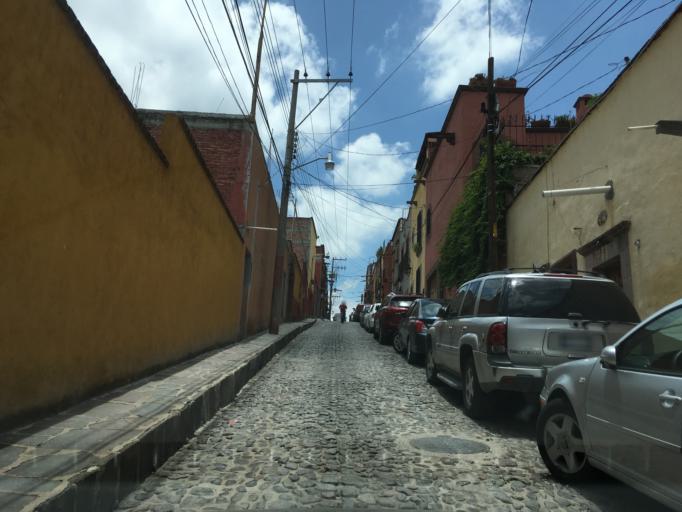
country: MX
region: Guanajuato
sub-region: San Miguel de Allende
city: San Miguel de Allende
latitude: 20.9140
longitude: -100.7481
